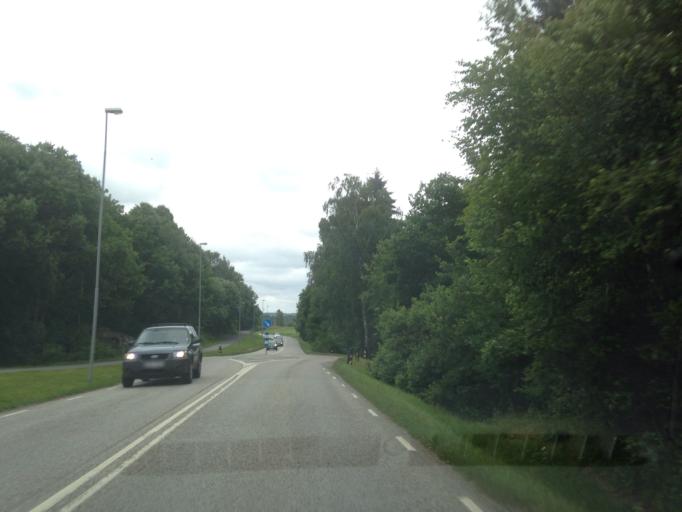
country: SE
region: Vaestra Goetaland
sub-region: Kungalvs Kommun
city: Kungalv
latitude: 57.8532
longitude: 11.8946
